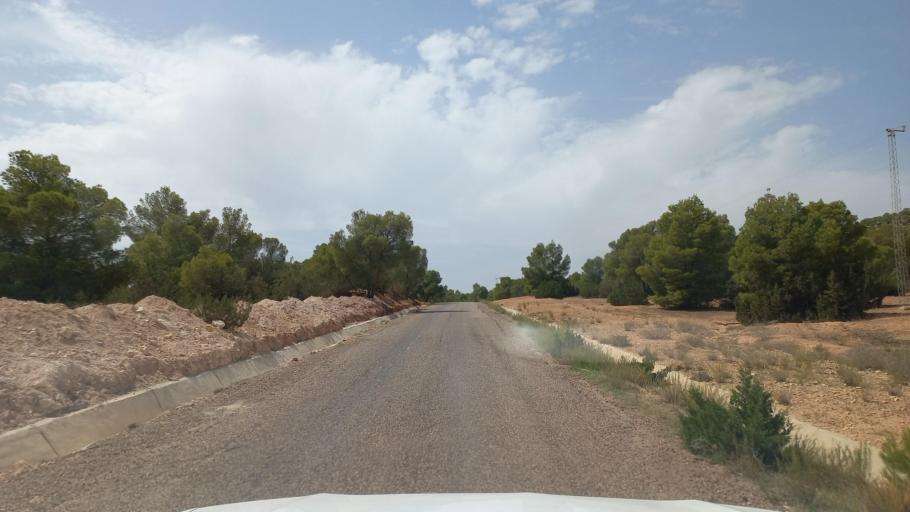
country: TN
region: Al Qasrayn
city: Kasserine
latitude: 35.3757
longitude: 8.9069
